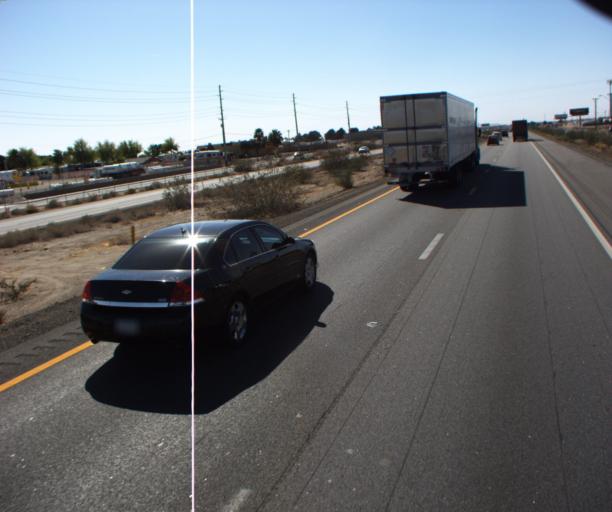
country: US
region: Arizona
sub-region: Yuma County
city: Fortuna Foothills
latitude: 32.6707
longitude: -114.4545
